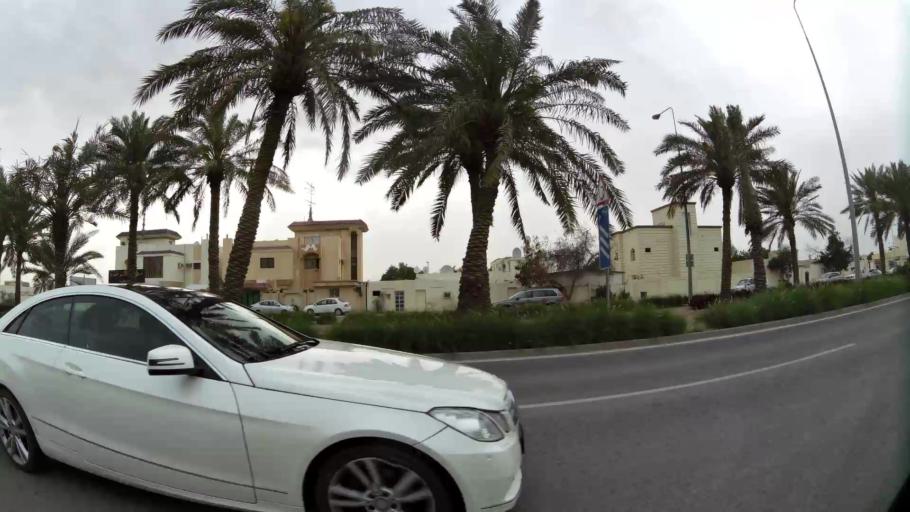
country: QA
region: Baladiyat ad Dawhah
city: Doha
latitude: 25.3121
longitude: 51.4874
